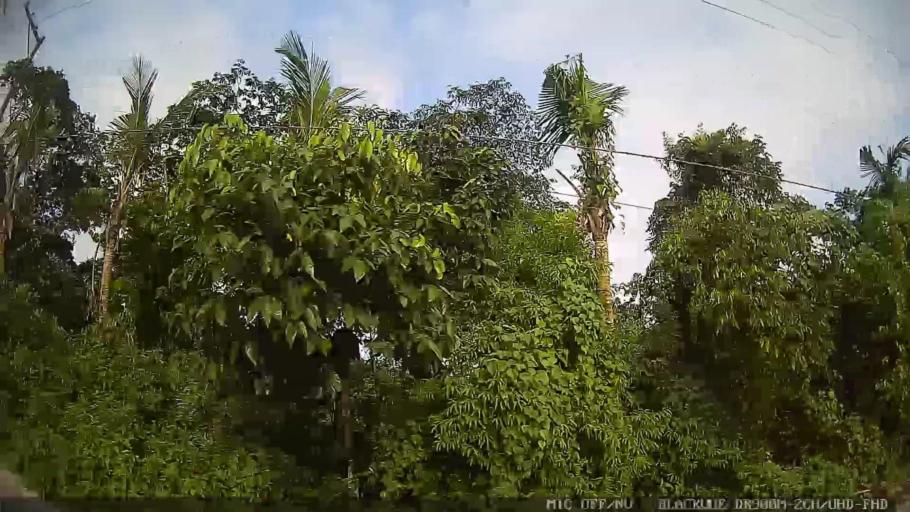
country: BR
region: Sao Paulo
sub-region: Guaruja
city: Guaruja
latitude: -23.9751
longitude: -46.2205
